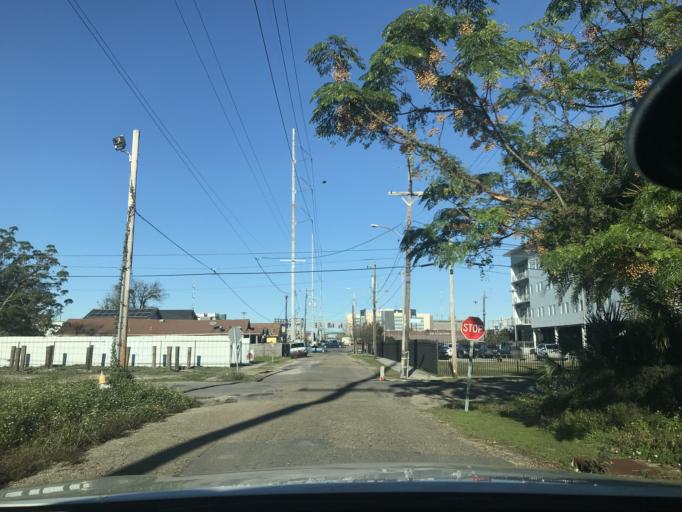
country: US
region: Louisiana
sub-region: Orleans Parish
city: New Orleans
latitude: 29.9555
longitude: -90.0994
